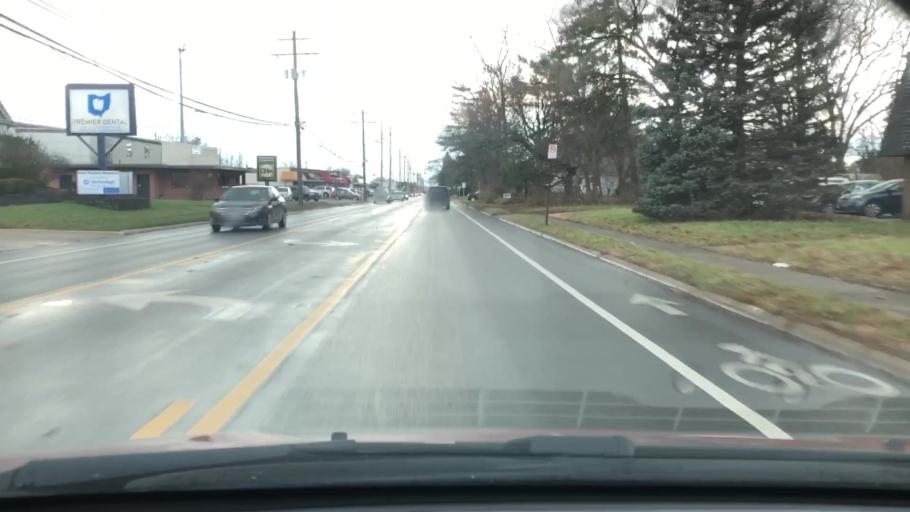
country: US
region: Ohio
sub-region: Franklin County
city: Worthington
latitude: 40.0566
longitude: -83.0006
